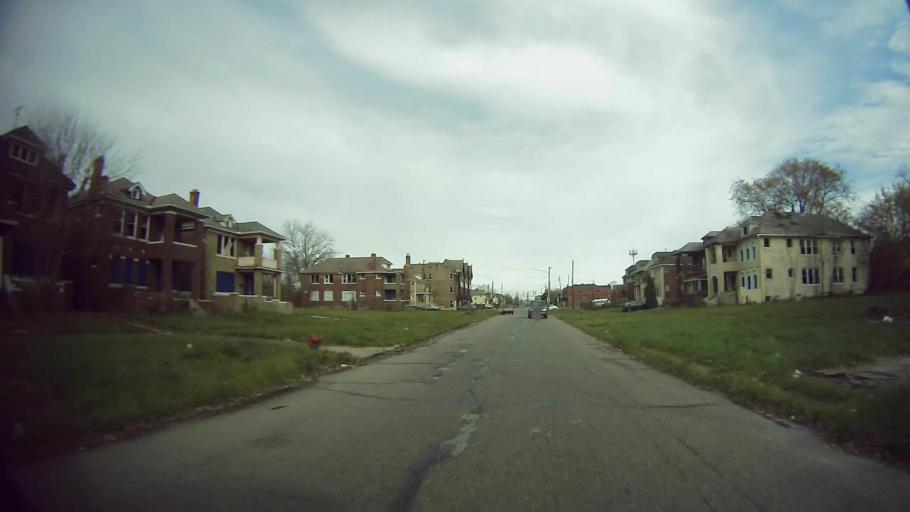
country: US
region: Michigan
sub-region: Wayne County
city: Highland Park
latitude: 42.3839
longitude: -83.1178
